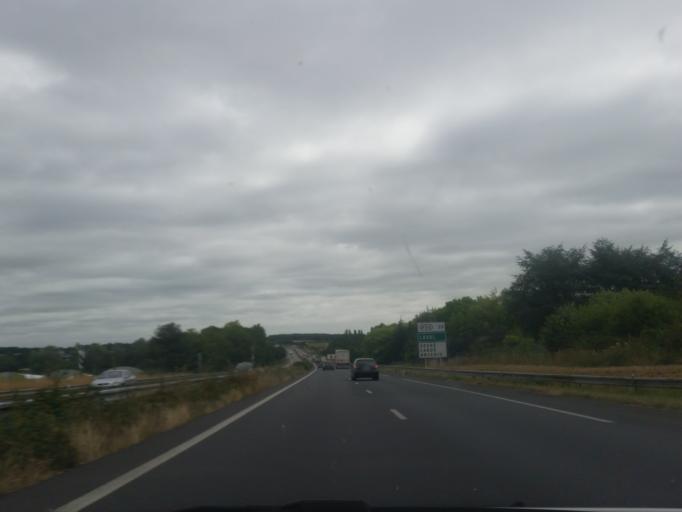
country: FR
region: Pays de la Loire
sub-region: Departement de la Loire-Atlantique
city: Carquefou
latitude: 47.2923
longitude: -1.4606
